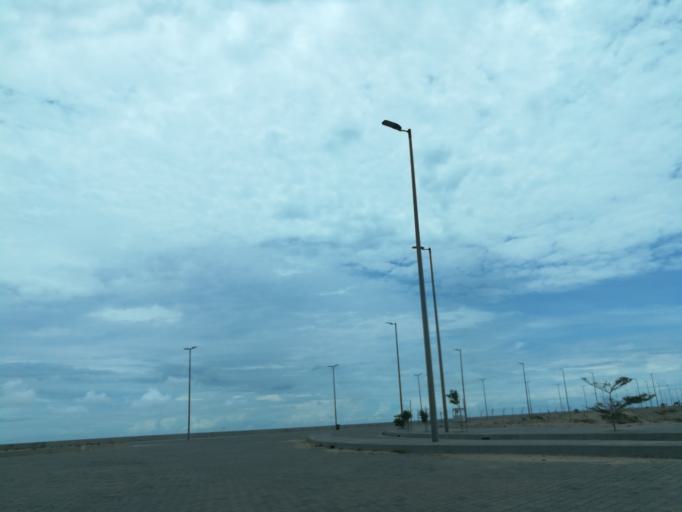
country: NG
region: Lagos
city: Ikoyi
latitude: 6.4063
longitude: 3.4190
